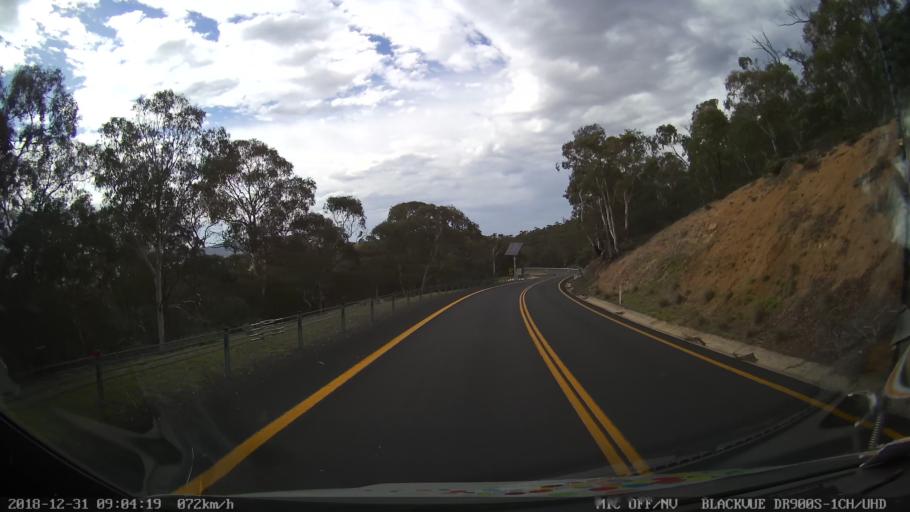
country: AU
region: New South Wales
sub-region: Snowy River
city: Jindabyne
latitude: -36.3529
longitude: 148.5863
